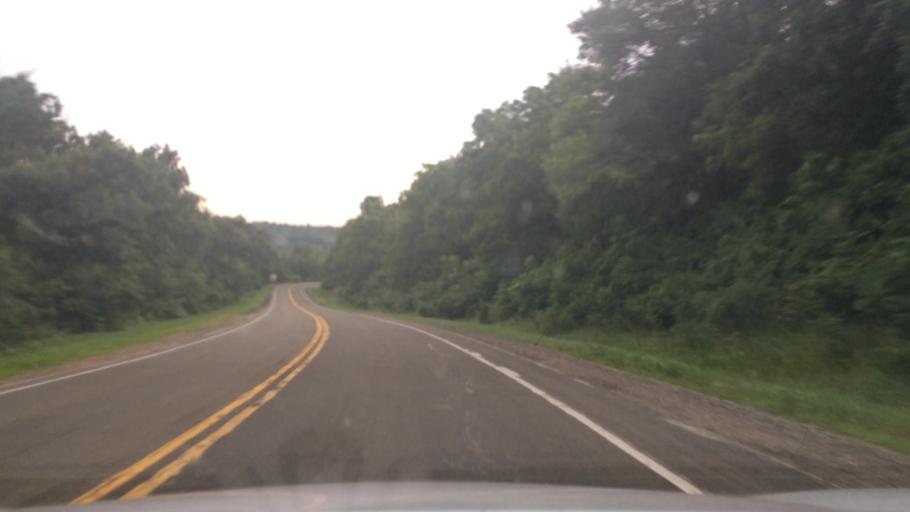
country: US
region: Wisconsin
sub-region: Columbia County
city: Lodi
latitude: 43.3220
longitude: -89.5021
